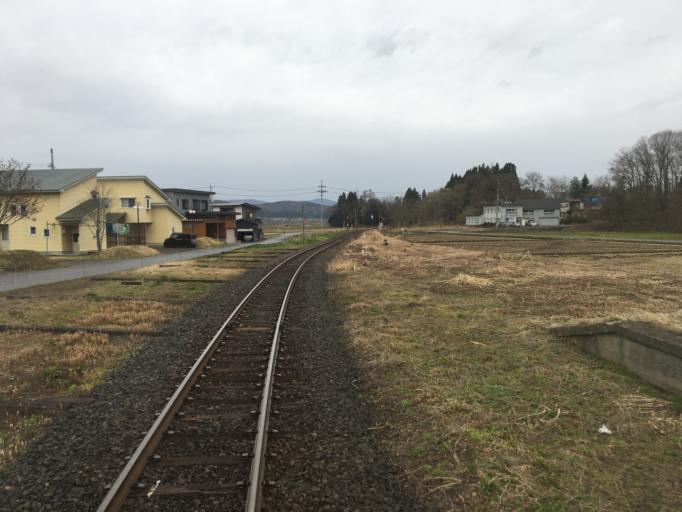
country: JP
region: Akita
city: Takanosu
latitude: 40.1283
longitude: 140.3727
